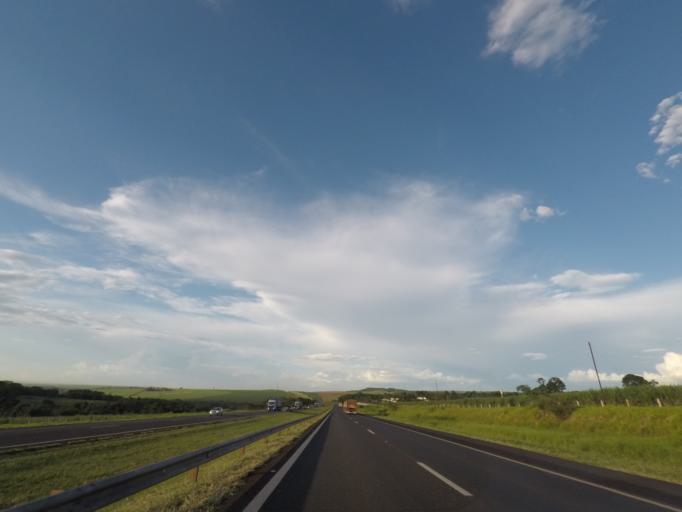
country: BR
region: Sao Paulo
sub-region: Ituverava
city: Ituverava
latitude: -20.2982
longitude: -47.7992
